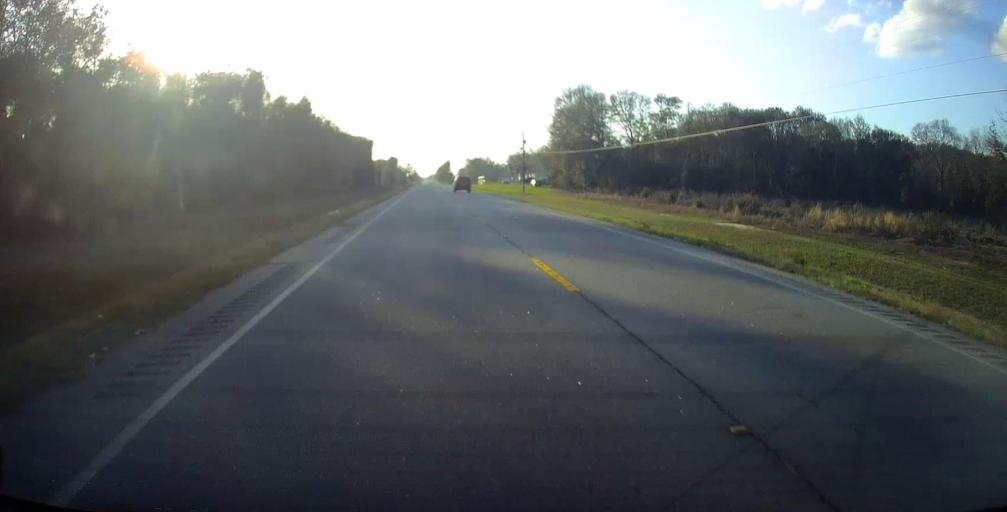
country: US
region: Georgia
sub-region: Bryan County
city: Pembroke
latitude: 32.1456
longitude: -81.7562
